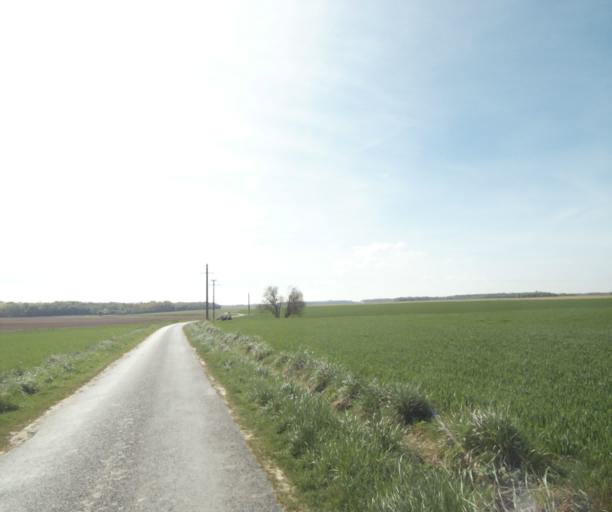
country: FR
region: Ile-de-France
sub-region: Departement de Seine-et-Marne
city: Nangis
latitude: 48.5477
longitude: 3.0348
